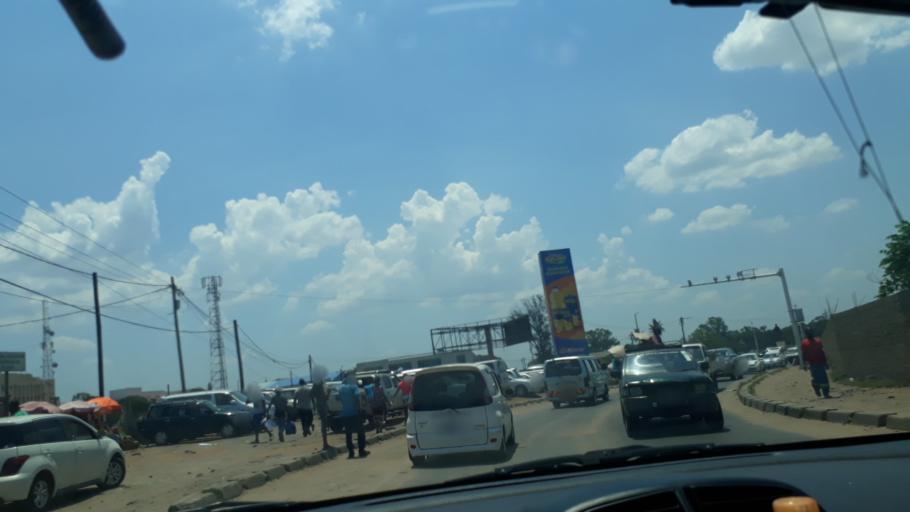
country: MZ
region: Maputo City
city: Maputo
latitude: -25.9355
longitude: 32.5518
